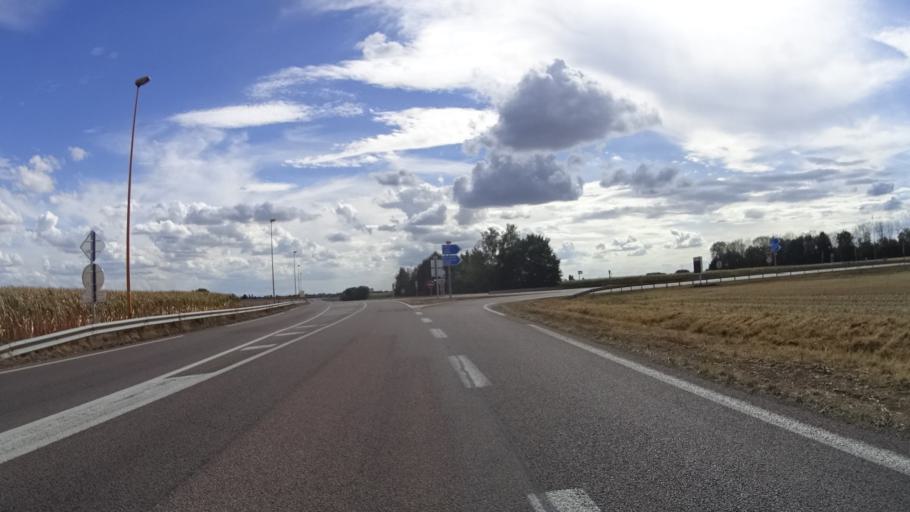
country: FR
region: Bourgogne
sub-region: Departement de la Cote-d'Or
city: Seurre
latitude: 47.0281
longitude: 5.1714
